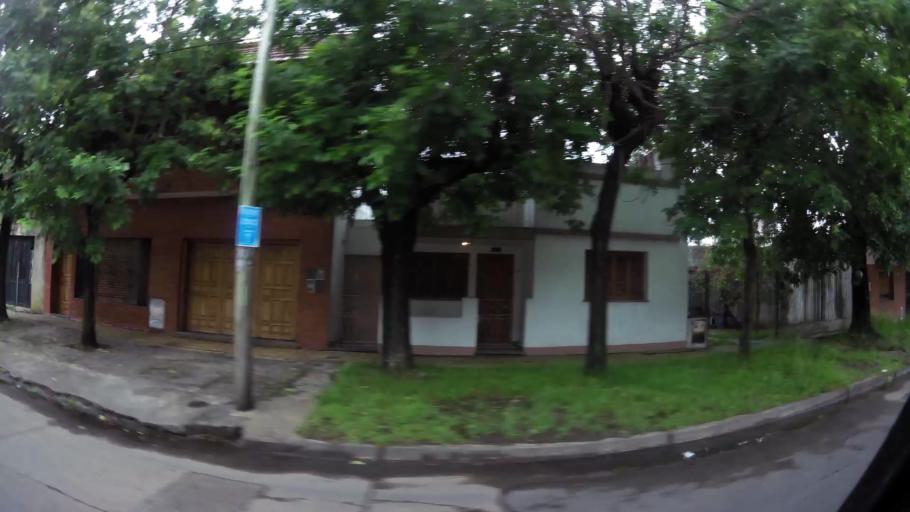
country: AR
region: Buenos Aires
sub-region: Partido de Lanus
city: Lanus
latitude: -34.7257
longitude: -58.3711
